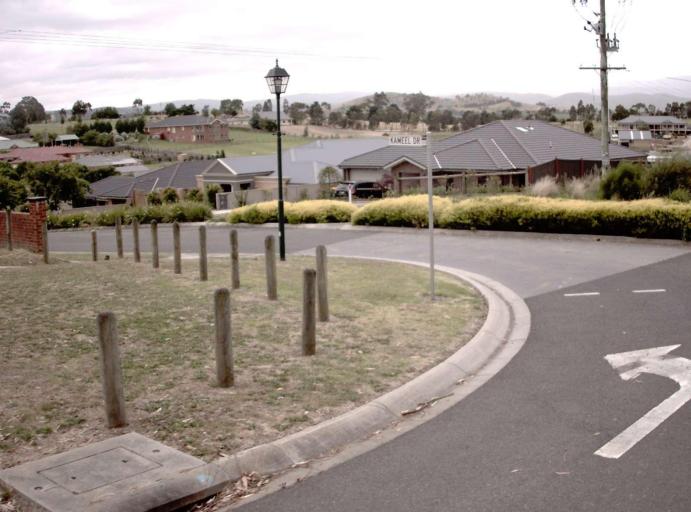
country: AU
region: Victoria
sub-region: Yarra Ranges
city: Yarra Glen
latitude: -37.6515
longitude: 145.3787
